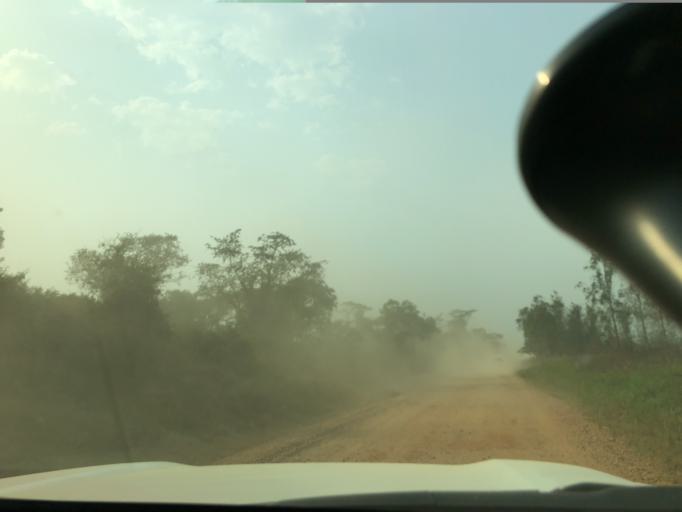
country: CD
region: Nord Kivu
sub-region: North Kivu
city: Butembo
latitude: 0.0858
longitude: 29.6445
